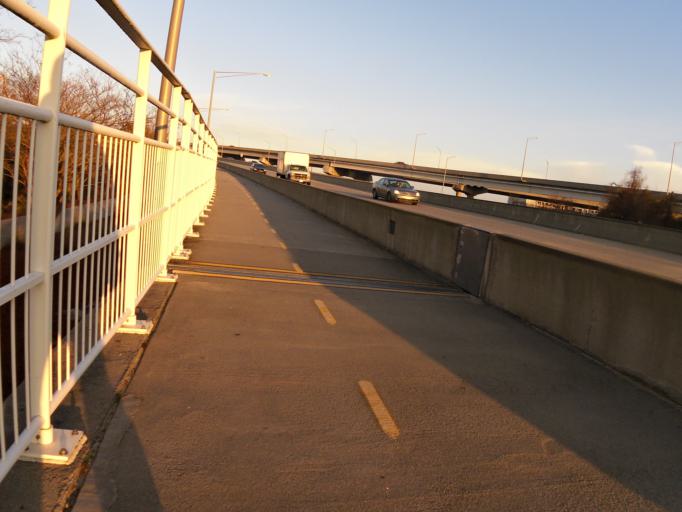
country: US
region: South Carolina
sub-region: Charleston County
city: Charleston
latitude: 32.7999
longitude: -79.9005
